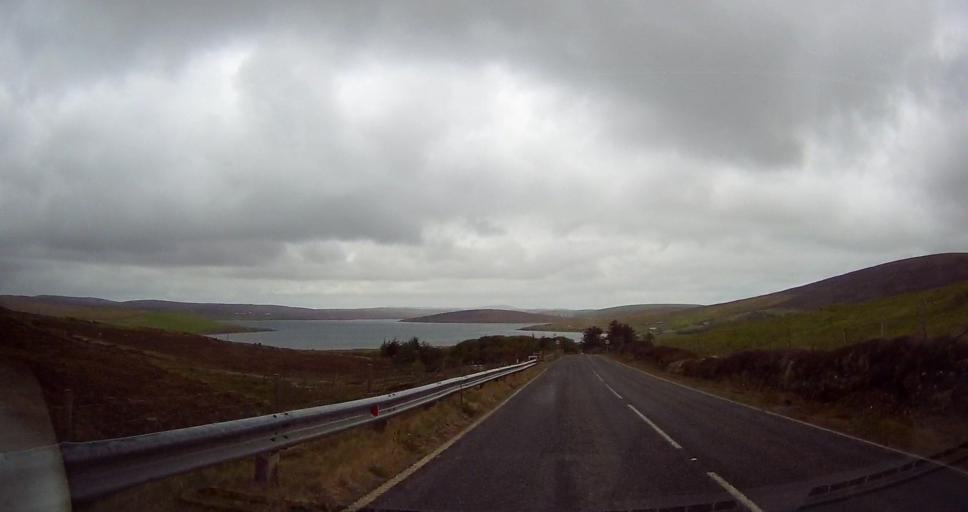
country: GB
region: Scotland
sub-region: Shetland Islands
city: Lerwick
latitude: 60.2409
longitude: -1.3384
